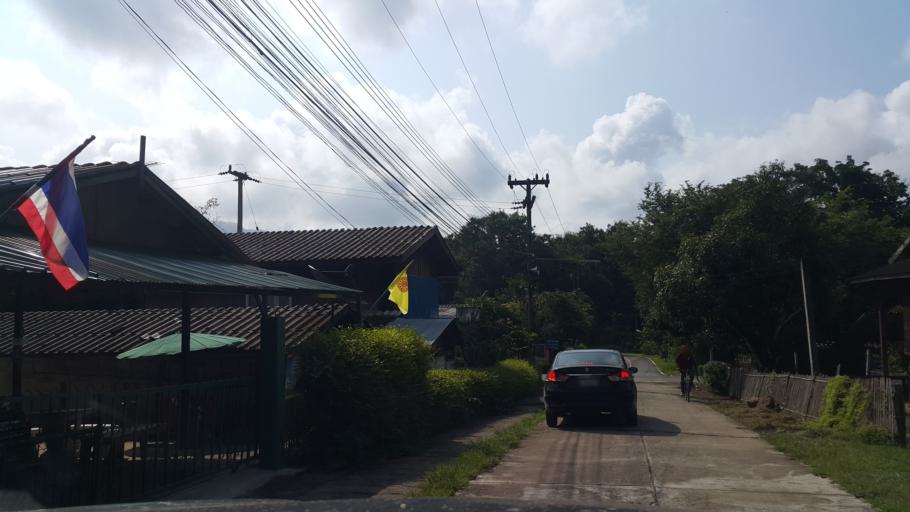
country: TH
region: Chiang Mai
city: Mae On
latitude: 18.7474
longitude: 99.2172
